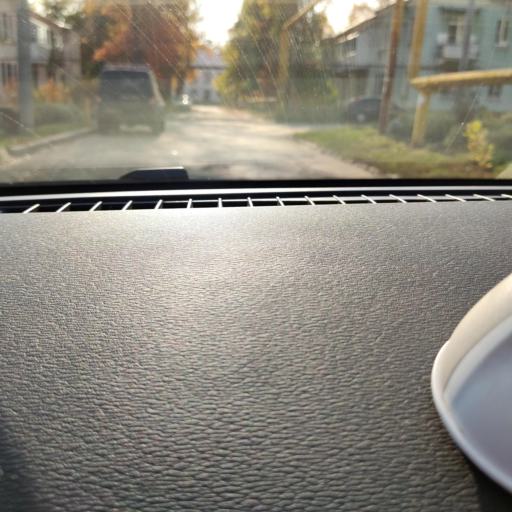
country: RU
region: Samara
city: Samara
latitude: 53.2662
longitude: 50.2382
